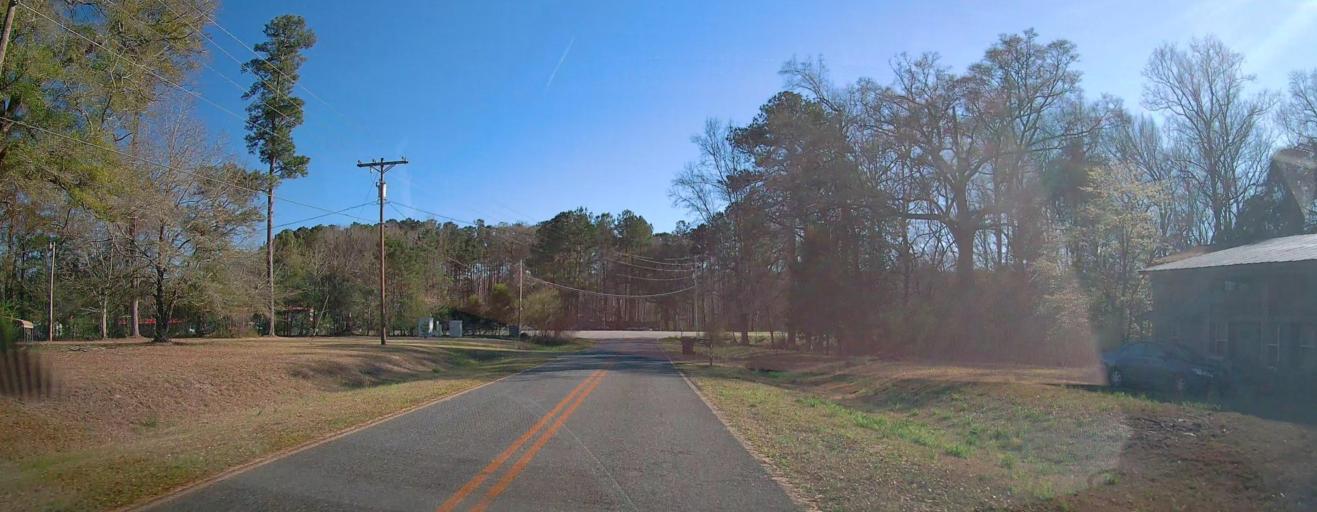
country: US
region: Georgia
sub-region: Peach County
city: Fort Valley
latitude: 32.5862
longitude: -83.8515
